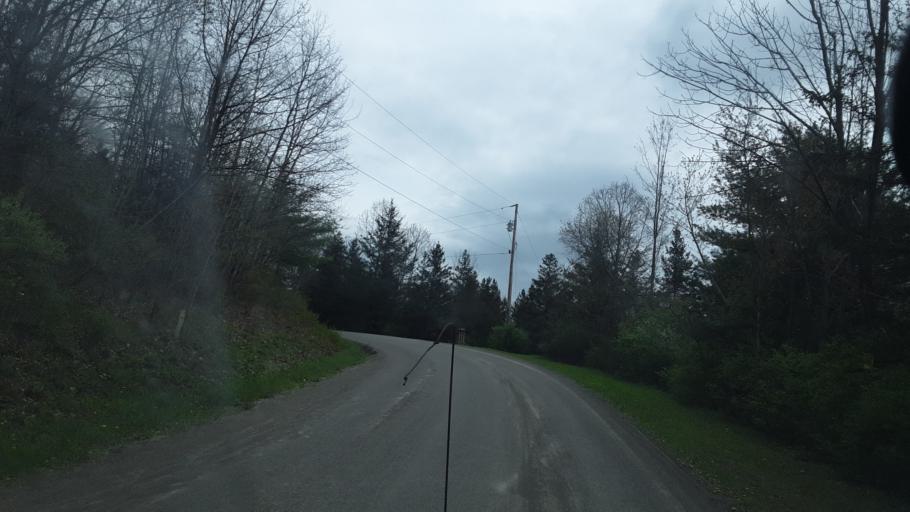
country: US
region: New York
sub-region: Steuben County
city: Addison
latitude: 42.0925
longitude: -77.3108
